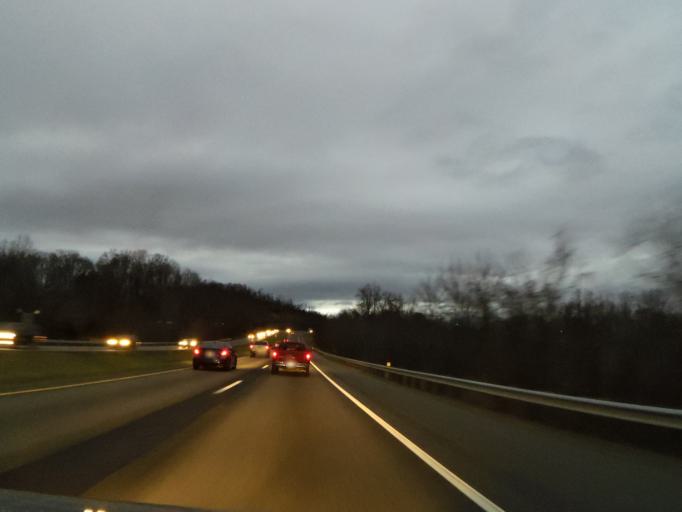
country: US
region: Tennessee
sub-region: Washington County
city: Oak Grove
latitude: 36.3859
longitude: -82.4341
